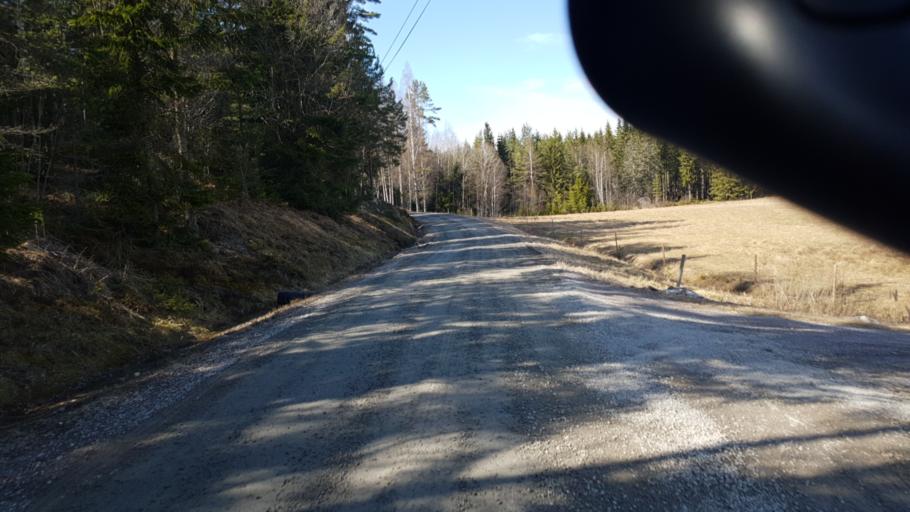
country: SE
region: Vaermland
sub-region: Arvika Kommun
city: Arvika
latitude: 59.6010
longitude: 12.7876
